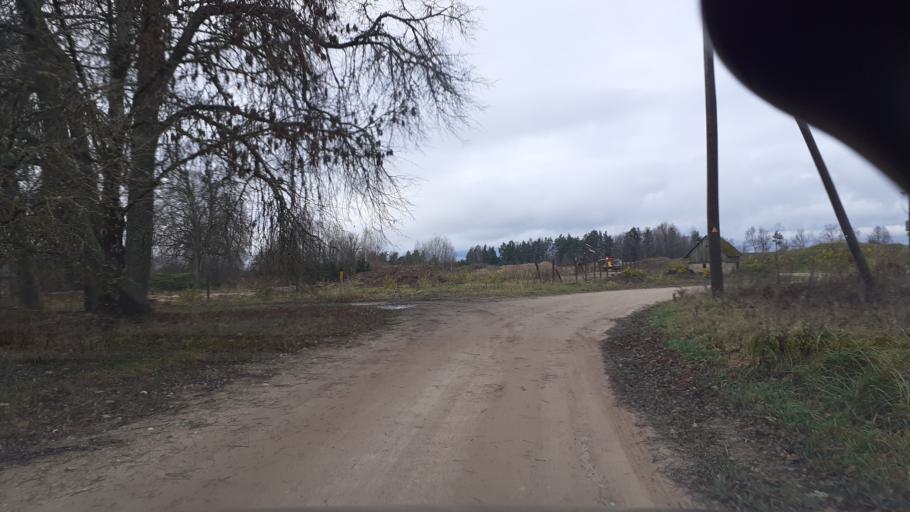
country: LV
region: Kuldigas Rajons
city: Kuldiga
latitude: 57.0454
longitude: 21.8693
